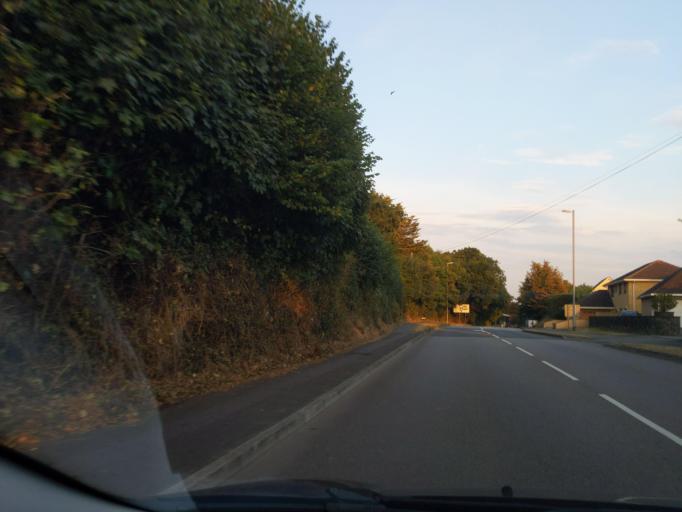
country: GB
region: England
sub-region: Cornwall
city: Liskeard
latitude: 50.4520
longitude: -4.4569
